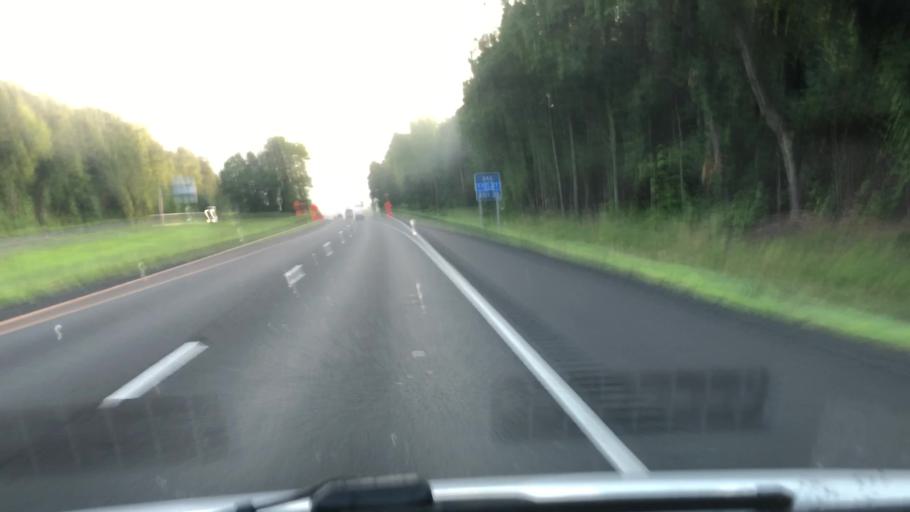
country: US
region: Massachusetts
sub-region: Hampshire County
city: Northampton
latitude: 42.3540
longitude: -72.6388
